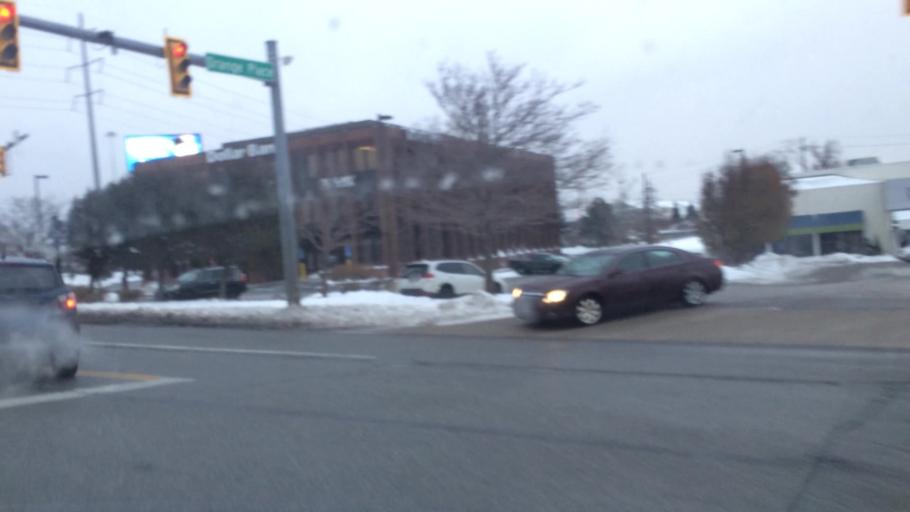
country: US
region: Ohio
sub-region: Cuyahoga County
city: Orange
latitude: 41.4623
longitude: -81.4880
